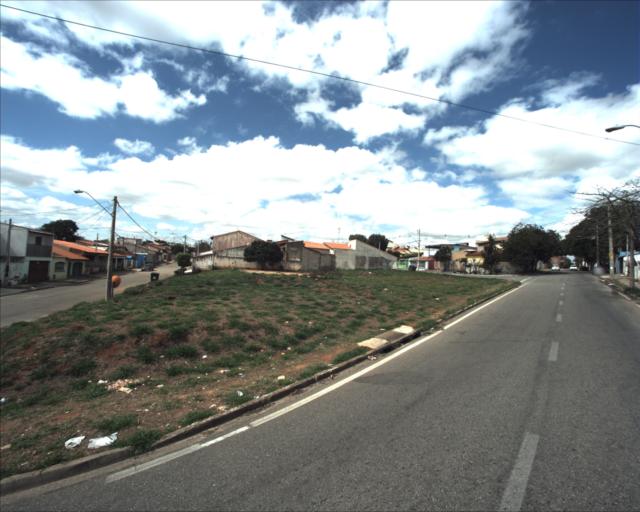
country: BR
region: Sao Paulo
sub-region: Sorocaba
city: Sorocaba
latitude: -23.5047
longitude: -47.5224
